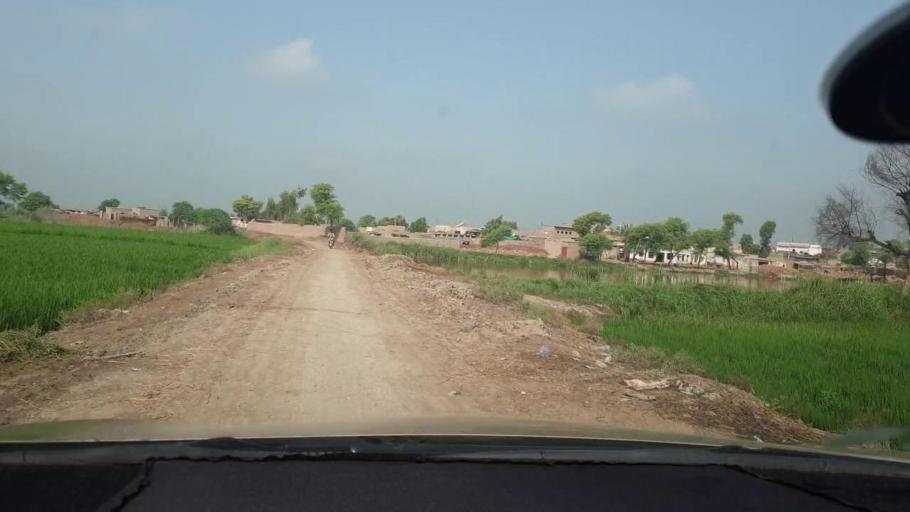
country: PK
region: Sindh
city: Kambar
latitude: 27.5417
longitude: 68.0491
